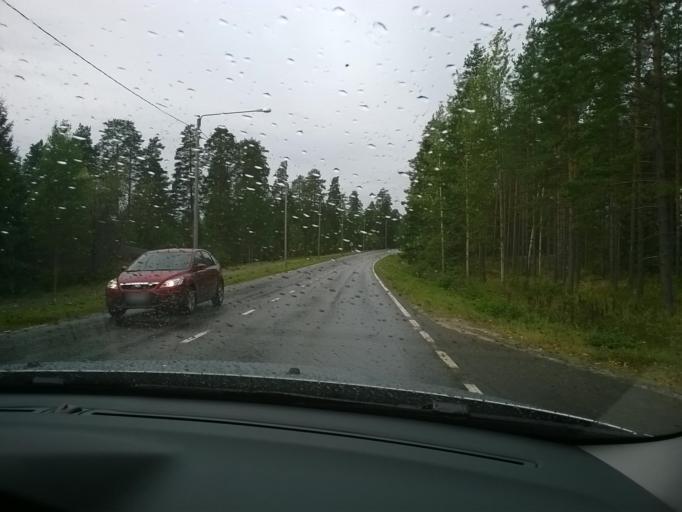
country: FI
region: Kainuu
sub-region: Kehys-Kainuu
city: Kuhmo
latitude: 64.1213
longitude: 29.5420
